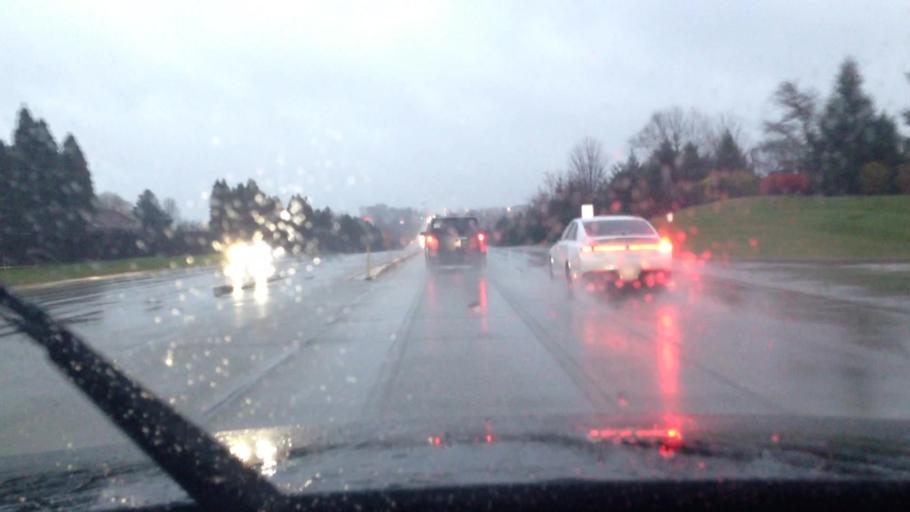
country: US
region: Illinois
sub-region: McHenry County
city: Lake in the Hills
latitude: 42.1756
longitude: -88.3546
